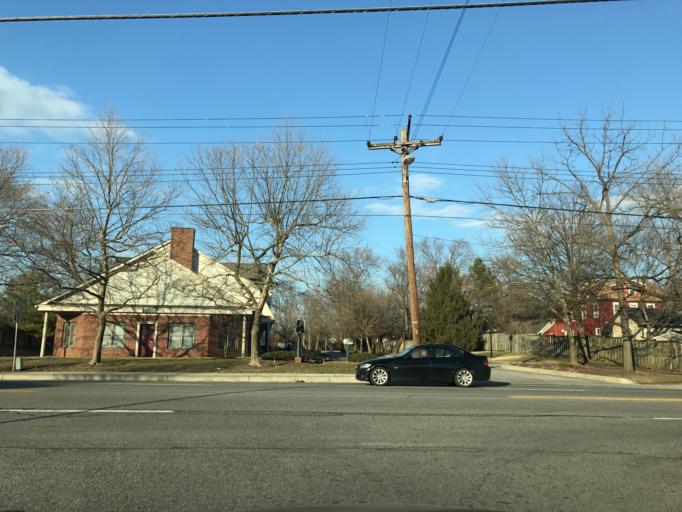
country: US
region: Maryland
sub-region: Anne Arundel County
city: Parole
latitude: 38.9792
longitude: -76.5188
